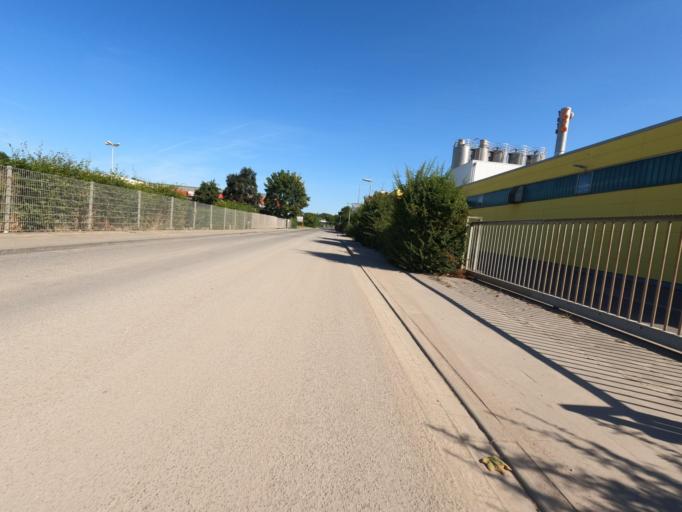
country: DE
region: North Rhine-Westphalia
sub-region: Regierungsbezirk Koln
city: Heinsberg
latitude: 51.0642
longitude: 6.1178
